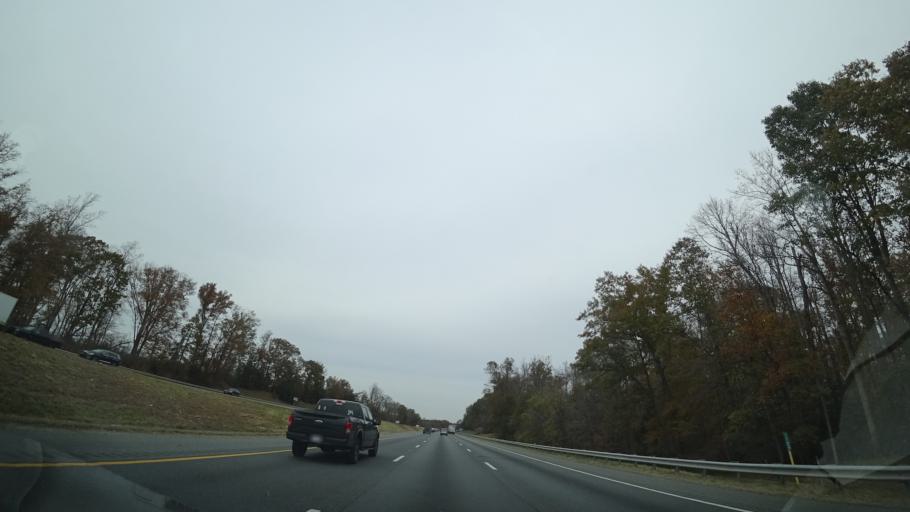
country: US
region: Virginia
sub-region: Spotsylvania County
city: Spotsylvania Courthouse
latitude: 38.1079
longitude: -77.5177
